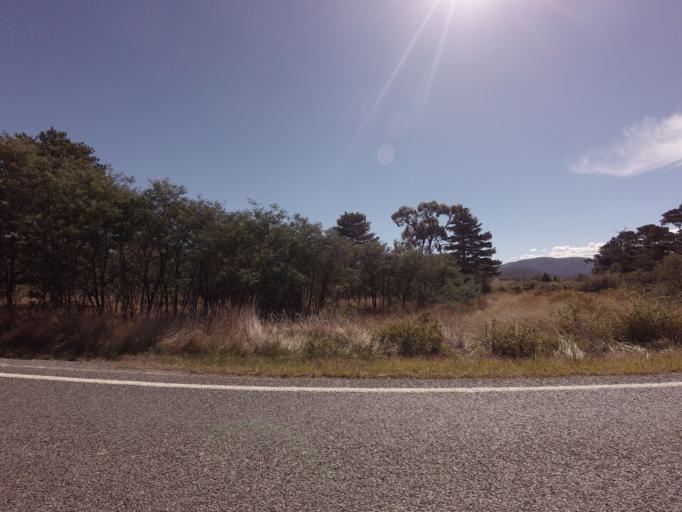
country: AU
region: Tasmania
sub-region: Northern Midlands
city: Evandale
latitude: -41.7870
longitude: 147.7153
